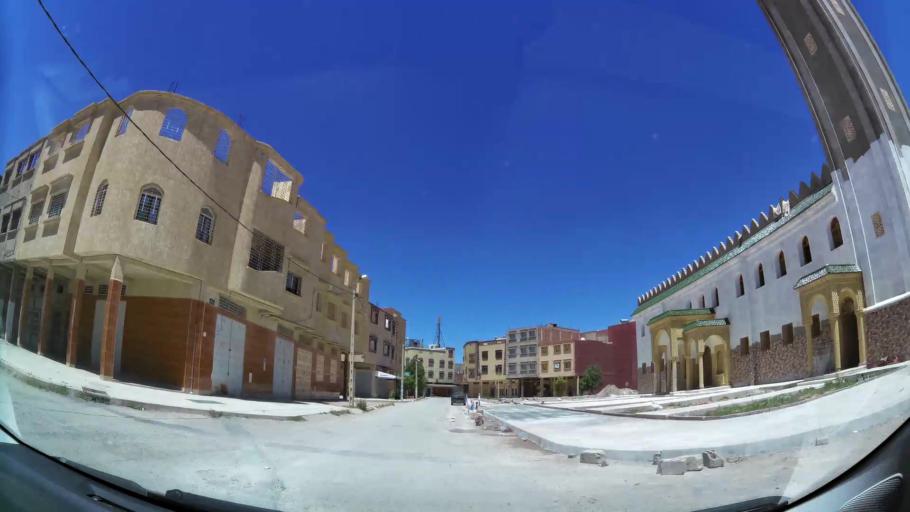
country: MA
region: Oriental
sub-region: Oujda-Angad
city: Oujda
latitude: 34.6760
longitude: -1.8715
